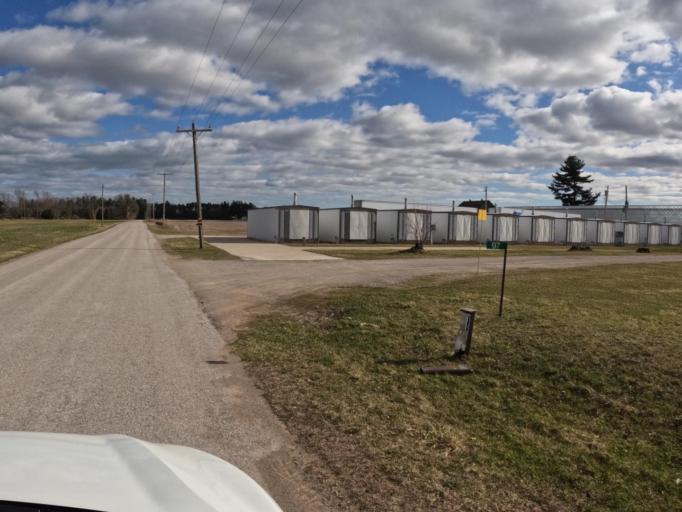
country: CA
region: Ontario
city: Norfolk County
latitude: 42.7451
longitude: -80.3820
